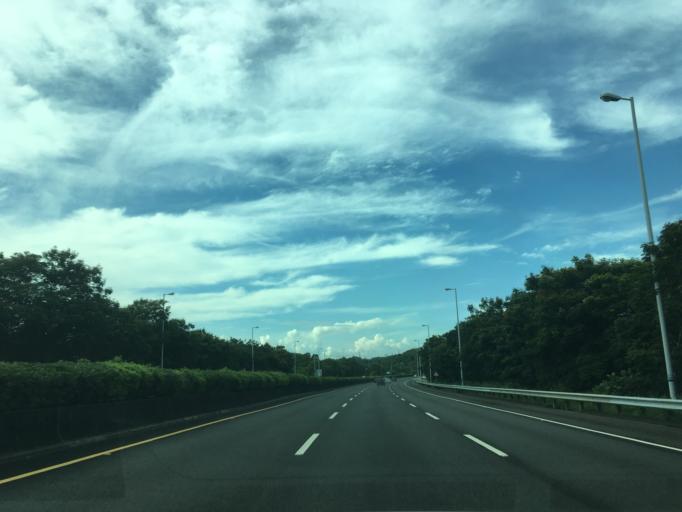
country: TW
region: Taiwan
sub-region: Chiayi
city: Jiayi Shi
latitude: 23.5205
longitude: 120.4849
